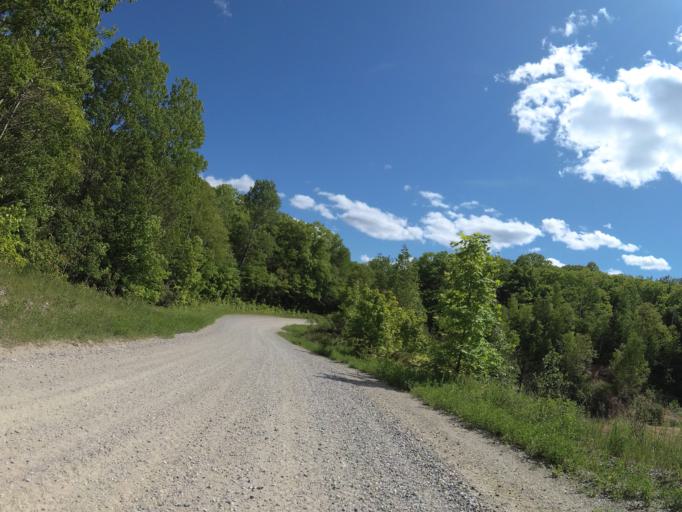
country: CA
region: Ontario
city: Renfrew
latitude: 45.0443
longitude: -76.8228
